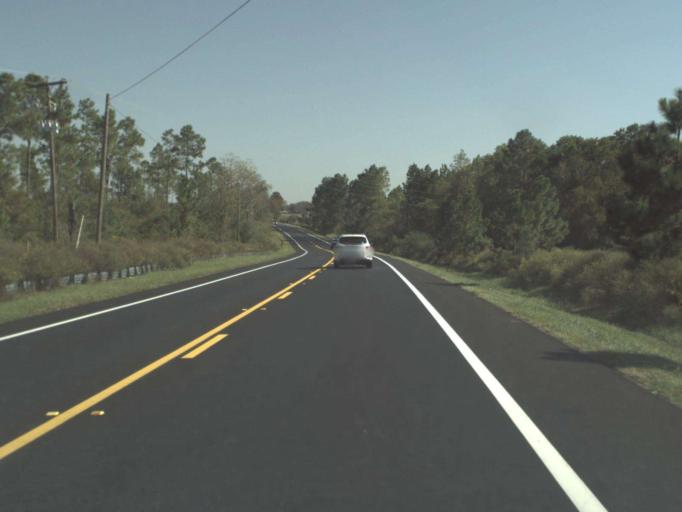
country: US
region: Alabama
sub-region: Covington County
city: Florala
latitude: 30.8862
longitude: -86.2770
